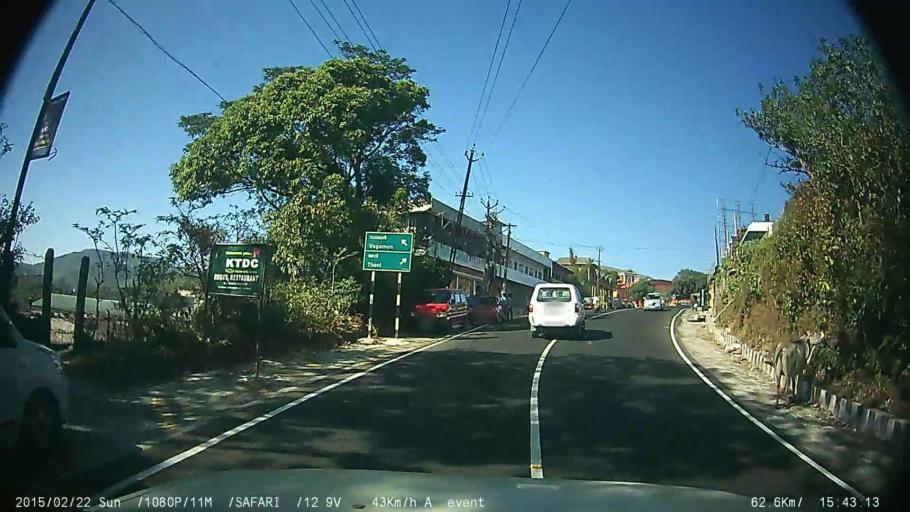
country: IN
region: Kerala
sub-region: Kottayam
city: Erattupetta
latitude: 9.5814
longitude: 76.9705
